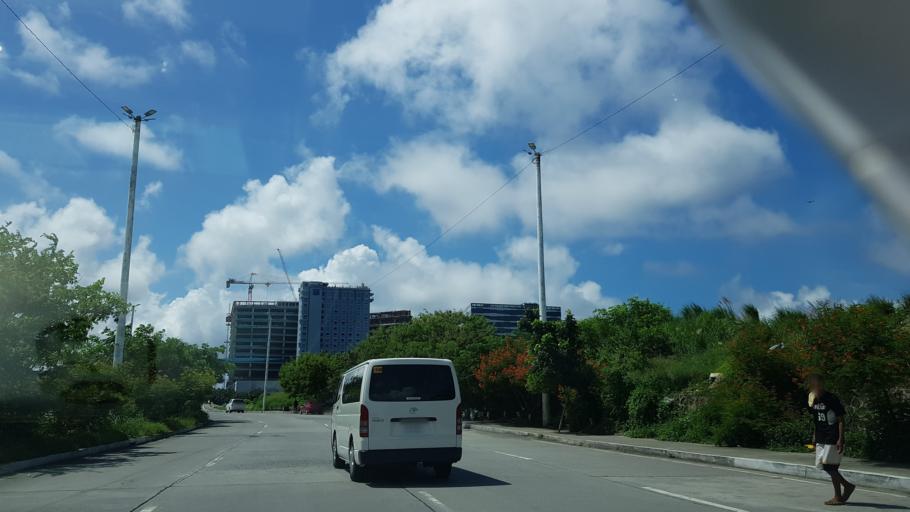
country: PH
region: Metro Manila
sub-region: City of Manila
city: Port Area
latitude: 14.5454
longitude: 120.9820
